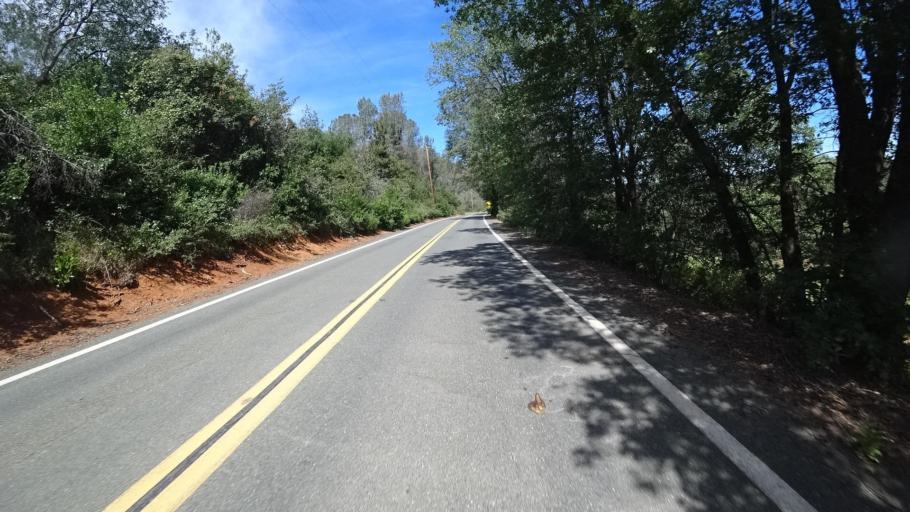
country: US
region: California
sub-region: Lake County
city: Lower Lake
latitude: 38.9140
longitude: -122.6537
